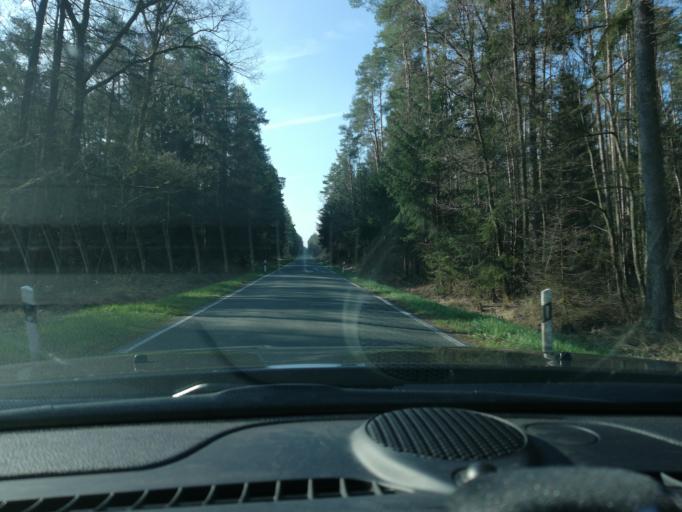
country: DE
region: Bavaria
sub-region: Regierungsbezirk Mittelfranken
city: Hessdorf
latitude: 49.6196
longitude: 10.9385
